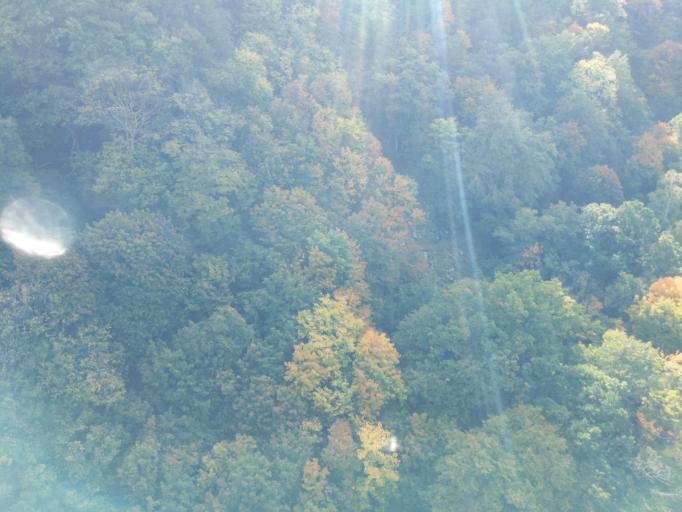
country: DE
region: Saxony-Anhalt
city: Thale
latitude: 51.7390
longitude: 11.0273
